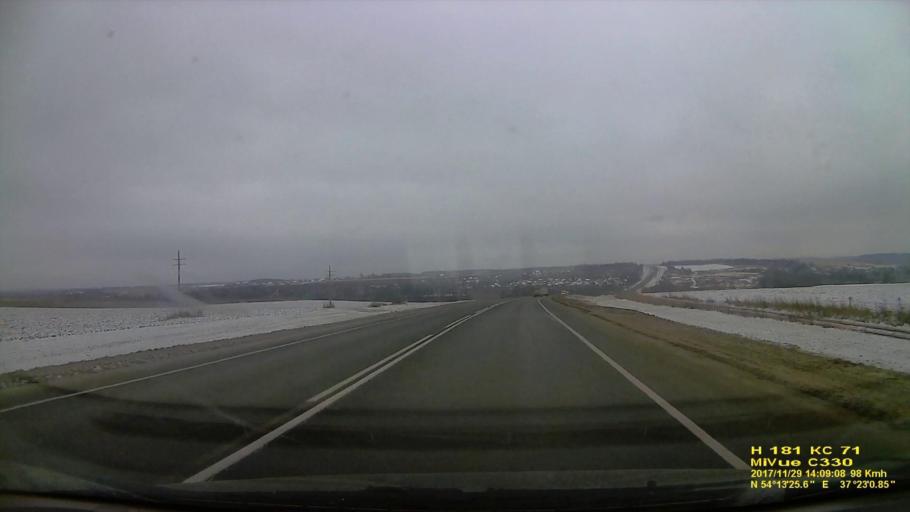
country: RU
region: Tula
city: Leninskiy
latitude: 54.2236
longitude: 37.3840
